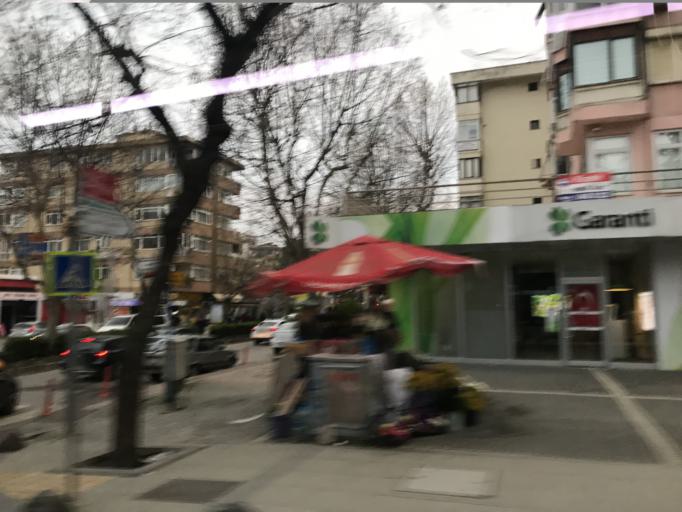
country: TR
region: Istanbul
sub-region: Atasehir
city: Atasehir
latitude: 40.9820
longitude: 29.0679
